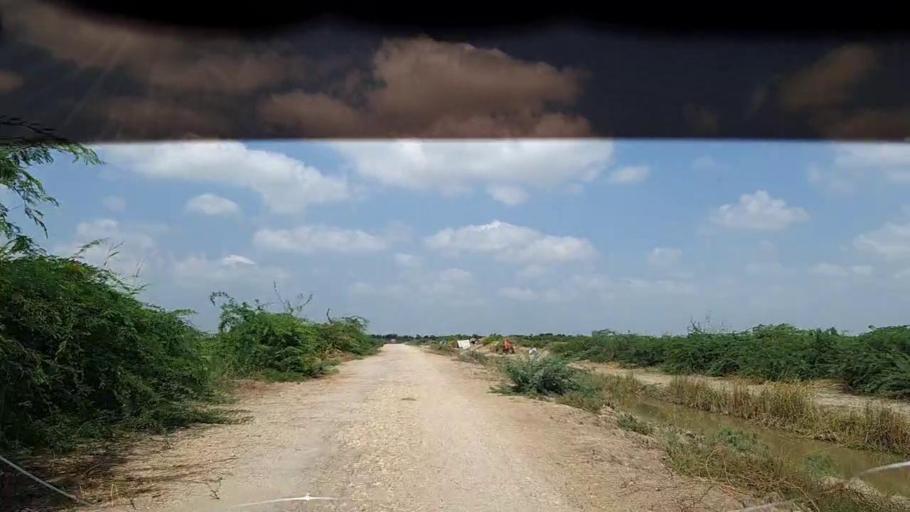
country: PK
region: Sindh
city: Kadhan
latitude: 24.5872
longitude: 68.9693
